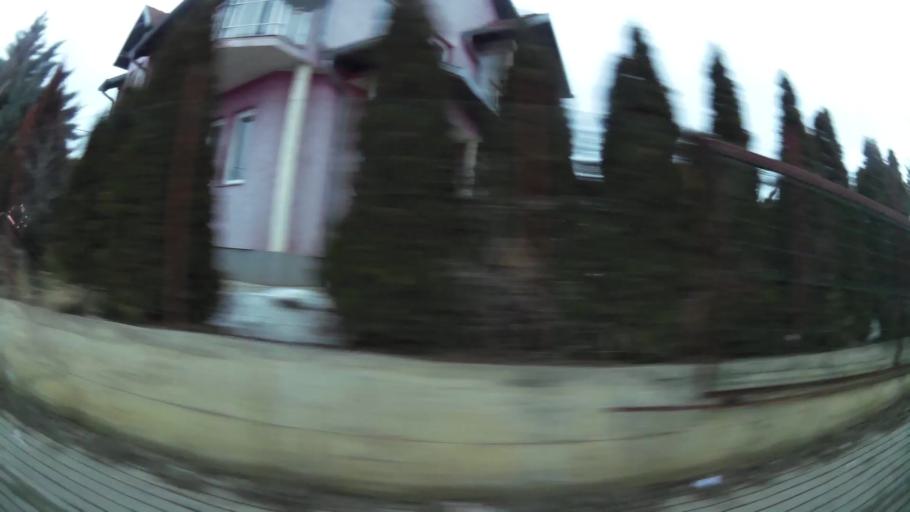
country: XK
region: Pristina
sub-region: Komuna e Prishtines
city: Pristina
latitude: 42.6328
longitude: 21.1680
